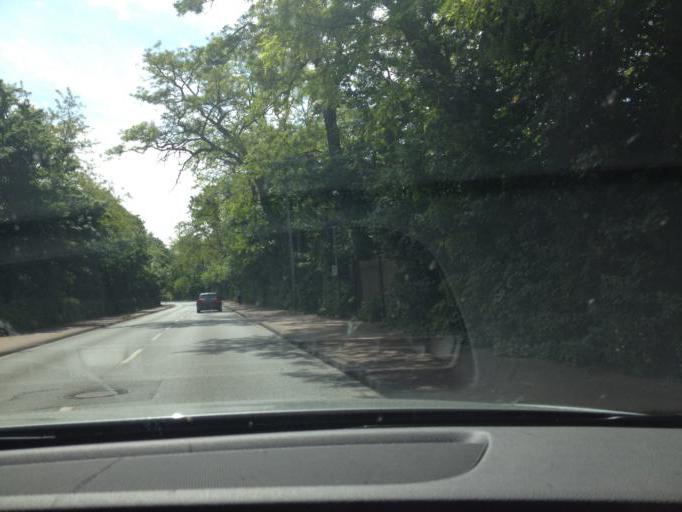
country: DE
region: North Rhine-Westphalia
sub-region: Regierungsbezirk Dusseldorf
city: Hochfeld
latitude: 51.3638
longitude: 6.7766
